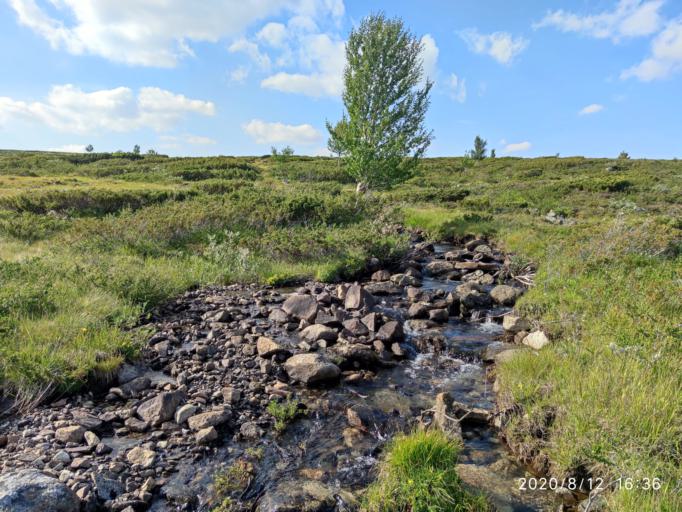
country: NO
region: Oppland
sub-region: Dovre
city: Dombas
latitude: 62.1652
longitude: 9.2826
